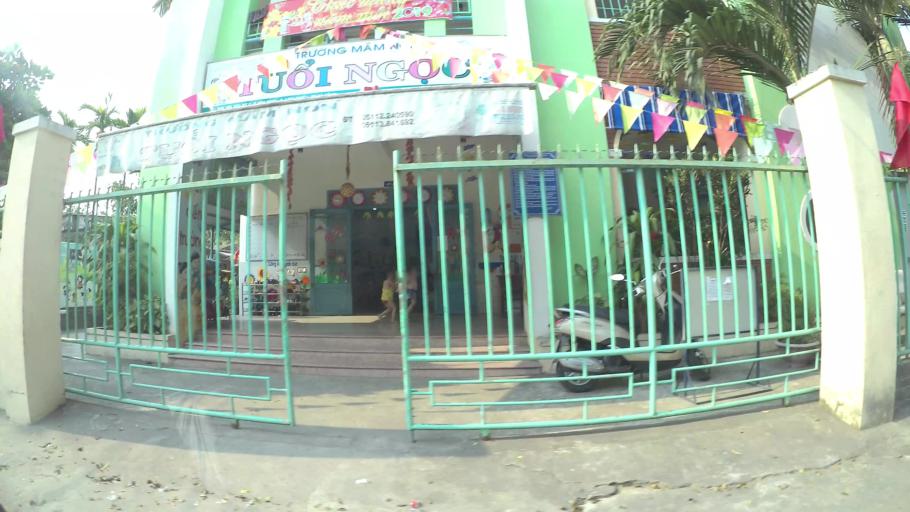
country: VN
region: Da Nang
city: Lien Chieu
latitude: 16.0517
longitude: 108.1693
